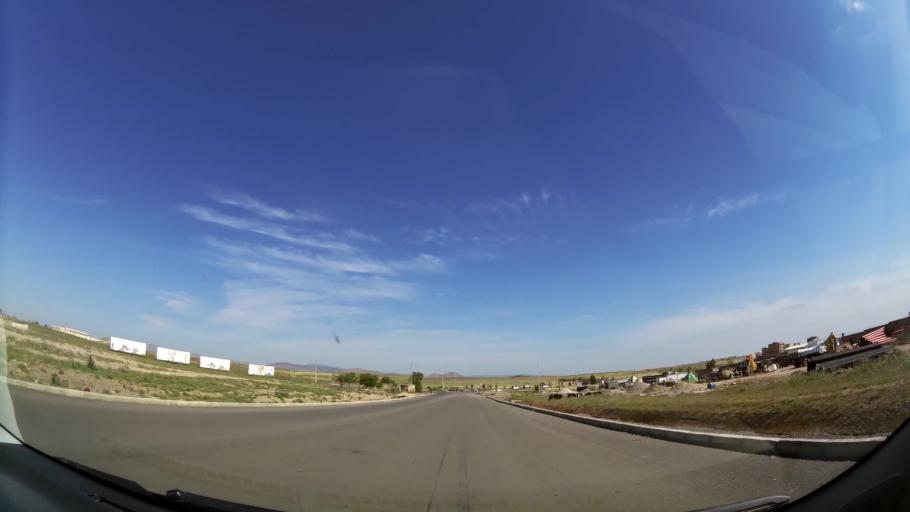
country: MA
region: Oriental
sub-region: Oujda-Angad
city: Oujda
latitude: 34.6529
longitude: -1.9553
